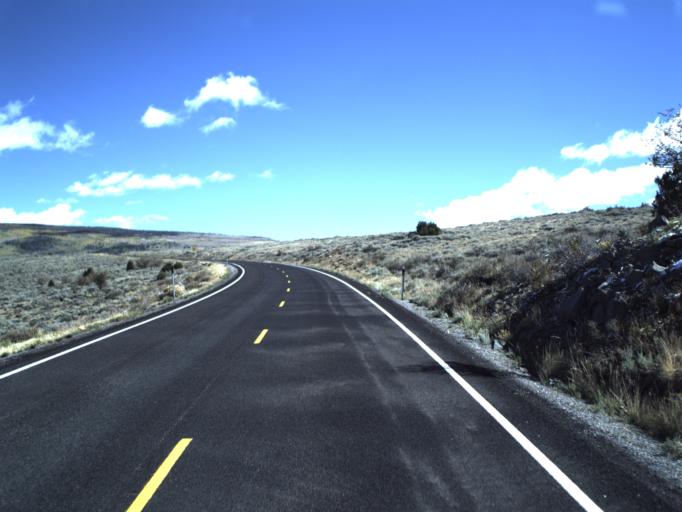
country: US
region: Utah
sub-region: Wayne County
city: Loa
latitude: 38.4936
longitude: -111.8122
